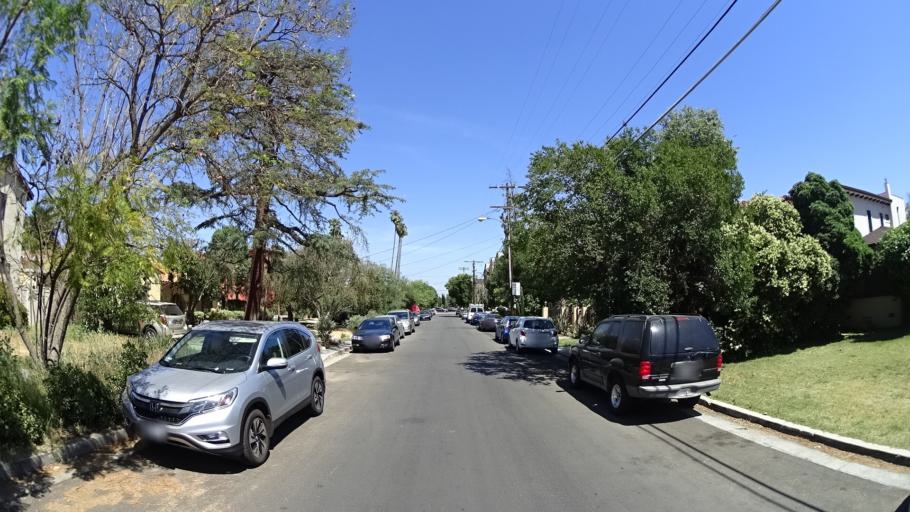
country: US
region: California
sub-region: Los Angeles County
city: North Hollywood
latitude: 34.1763
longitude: -118.3980
